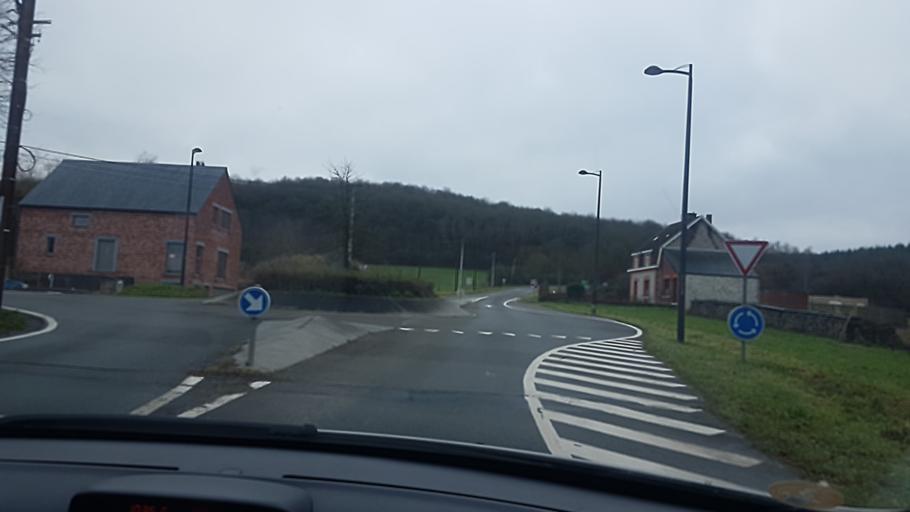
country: BE
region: Wallonia
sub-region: Province de Namur
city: Couvin
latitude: 50.0657
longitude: 4.6084
